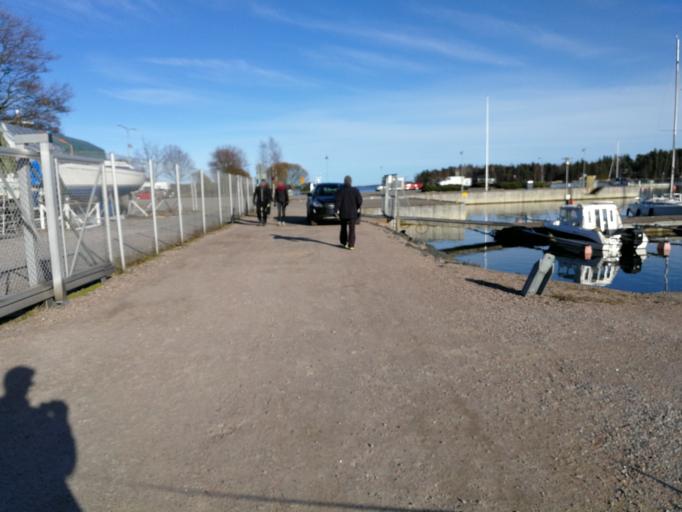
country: FI
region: Uusimaa
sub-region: Helsinki
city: Vantaa
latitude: 60.1995
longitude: 25.1396
